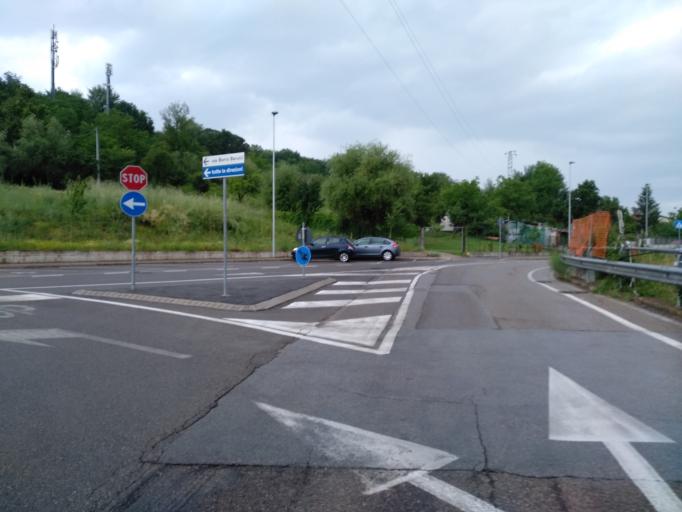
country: IT
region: Tuscany
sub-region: Province of Arezzo
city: San Giovanni Valdarno
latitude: 43.5627
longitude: 11.5283
